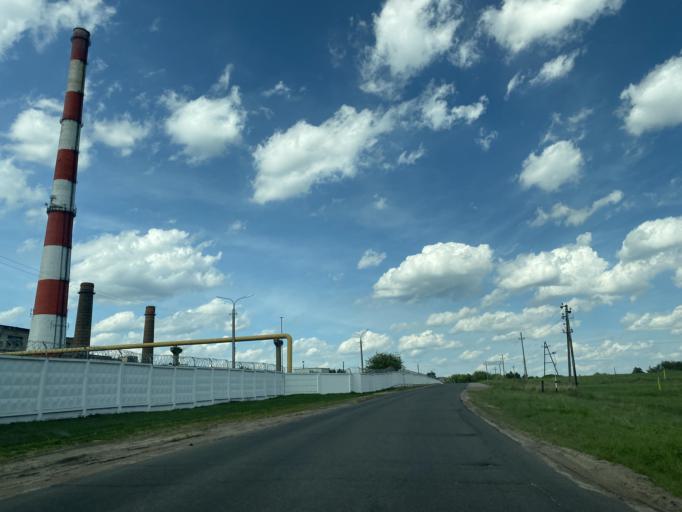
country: BY
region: Minsk
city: Horad Zhodzina
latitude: 54.0914
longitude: 28.3521
